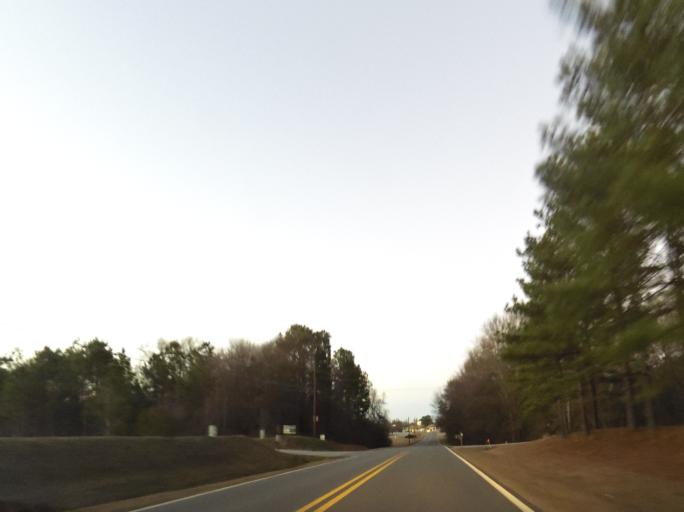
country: US
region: Georgia
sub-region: Peach County
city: Byron
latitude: 32.6452
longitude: -83.7572
